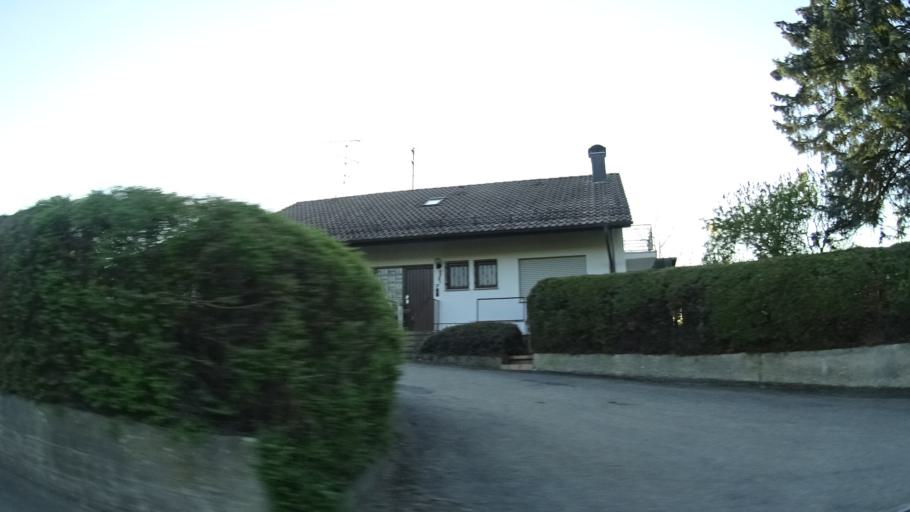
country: DE
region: Baden-Wuerttemberg
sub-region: Regierungsbezirk Stuttgart
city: Pfedelbach
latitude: 49.1566
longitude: 9.4972
